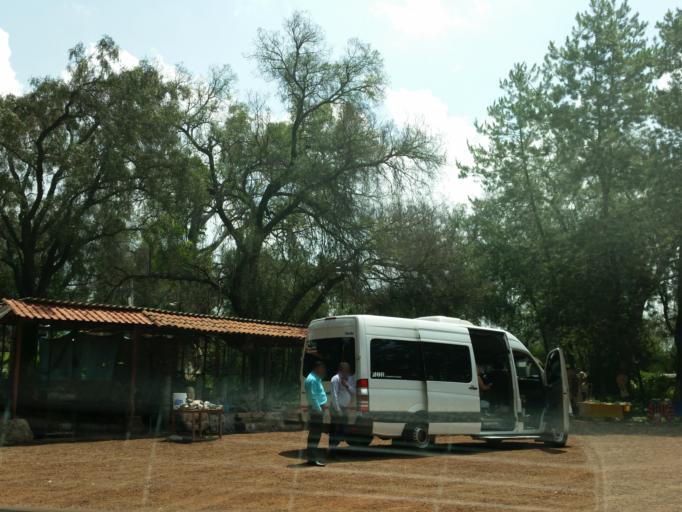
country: MX
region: Mexico
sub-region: Teotihuacan
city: Teotihuacan de Arista
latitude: 19.6869
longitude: -98.8524
